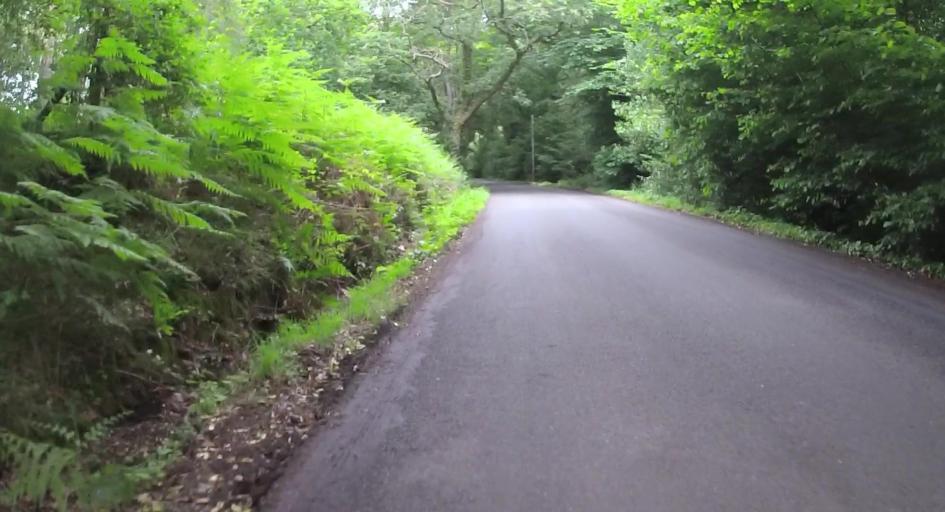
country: GB
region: England
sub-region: Bracknell Forest
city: Crowthorne
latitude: 51.3891
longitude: -0.8080
